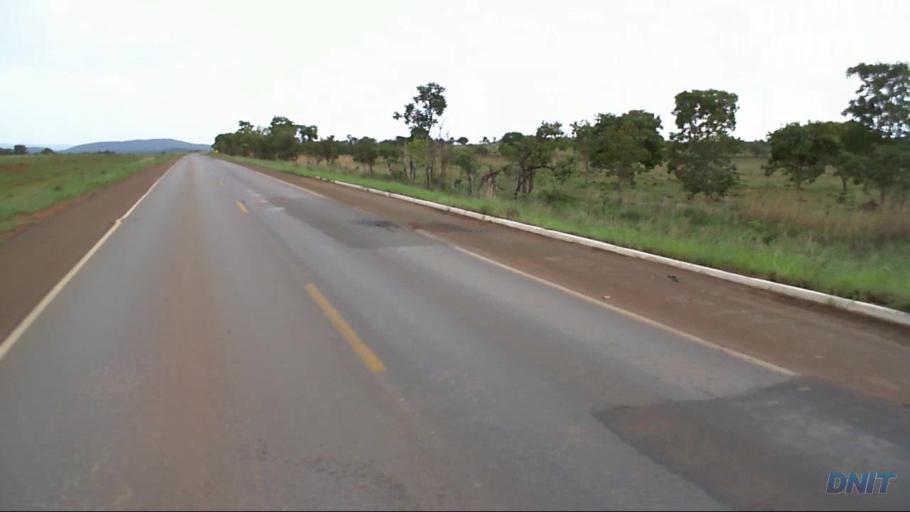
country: BR
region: Goias
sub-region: Barro Alto
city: Barro Alto
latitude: -14.8613
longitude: -49.0192
